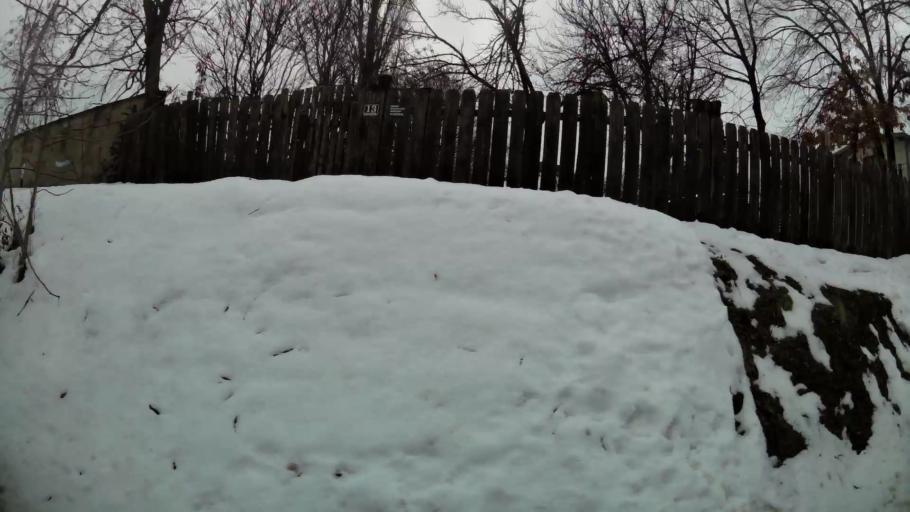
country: RS
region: Central Serbia
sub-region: Belgrade
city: Zemun
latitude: 44.8345
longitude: 20.3794
